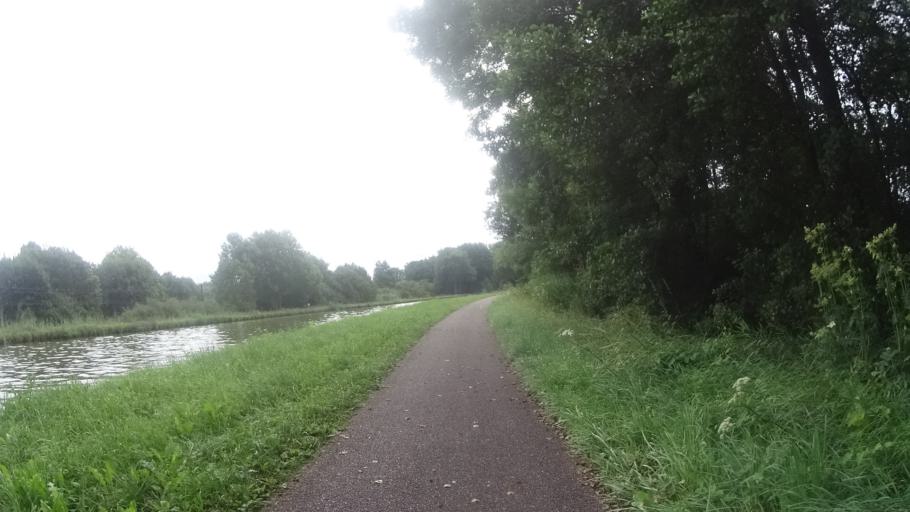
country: FR
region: Alsace
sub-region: Departement du Bas-Rhin
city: Dettwiller
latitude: 48.7590
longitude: 7.4444
